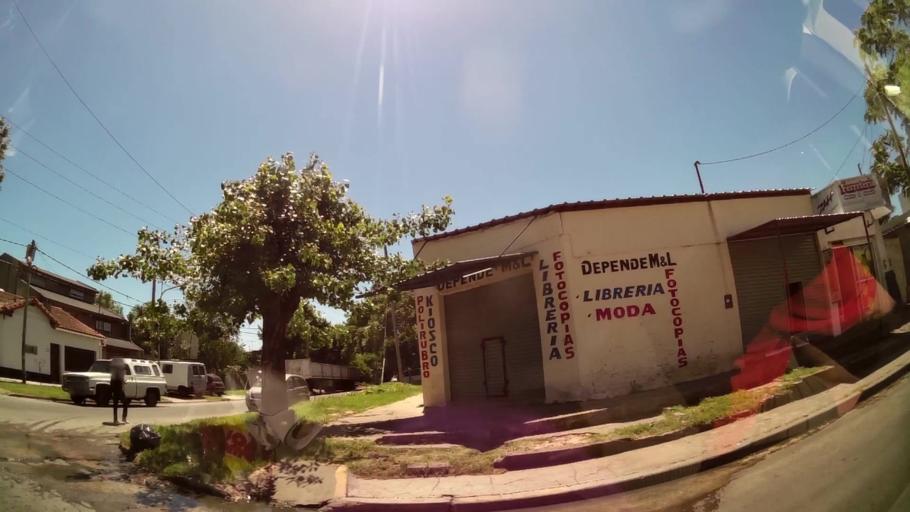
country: AR
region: Buenos Aires
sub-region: Partido de Tigre
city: Tigre
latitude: -34.4855
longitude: -58.6359
